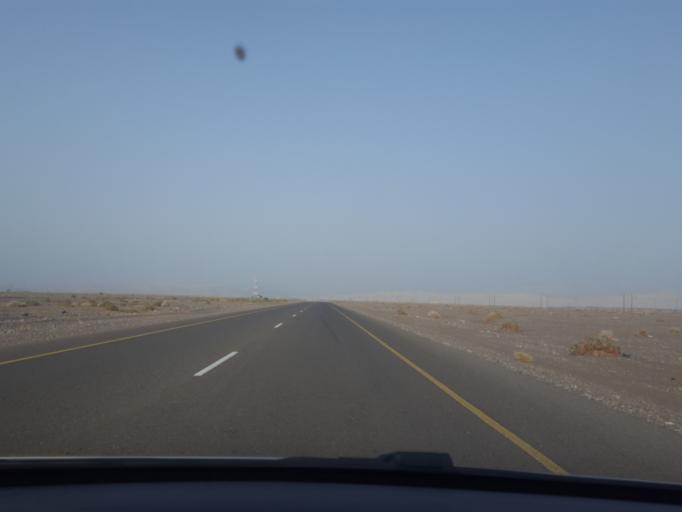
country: AE
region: Abu Dhabi
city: Al Ain
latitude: 24.0124
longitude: 55.9415
